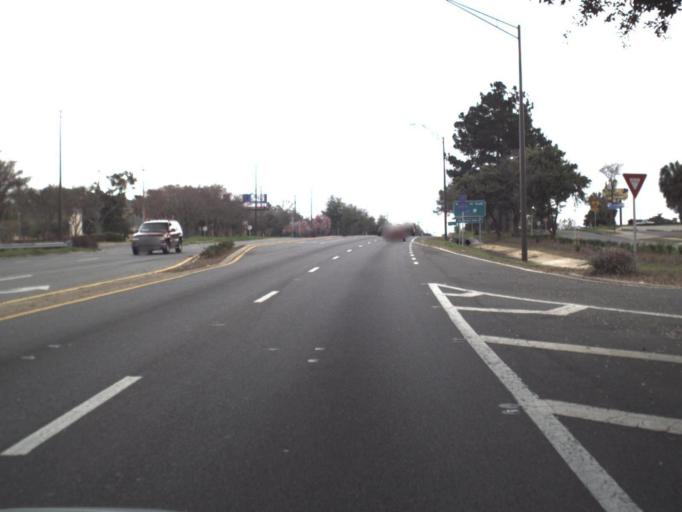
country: US
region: Florida
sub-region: Leon County
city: Tallahassee
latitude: 30.4380
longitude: -84.2678
